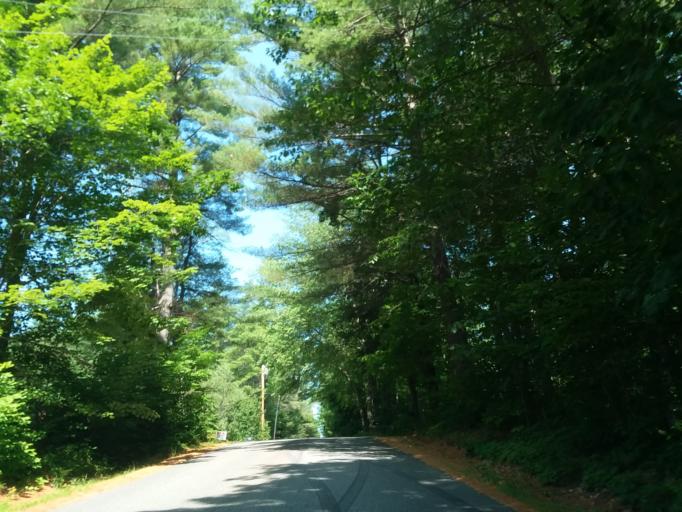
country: US
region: Maine
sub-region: Kennebec County
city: Winthrop
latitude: 44.2794
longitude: -70.0147
